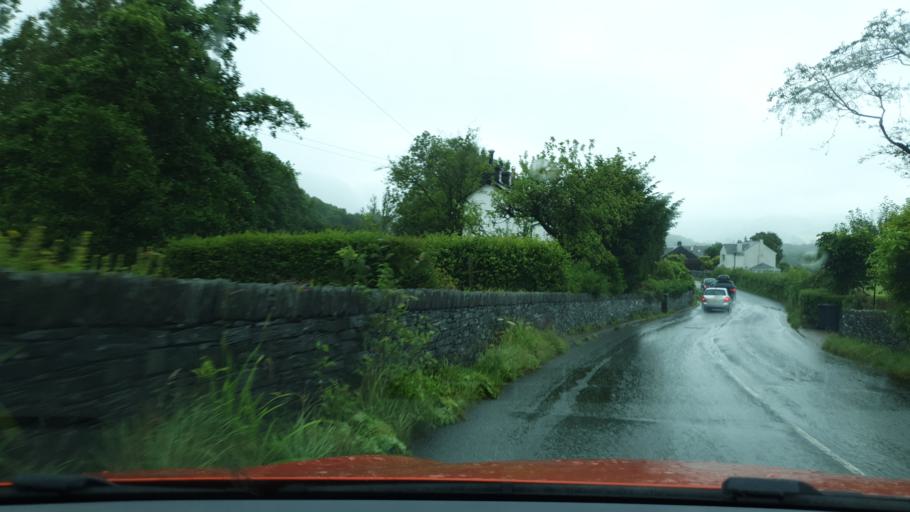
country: GB
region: England
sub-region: Cumbria
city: Ambleside
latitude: 54.3577
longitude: -3.0817
